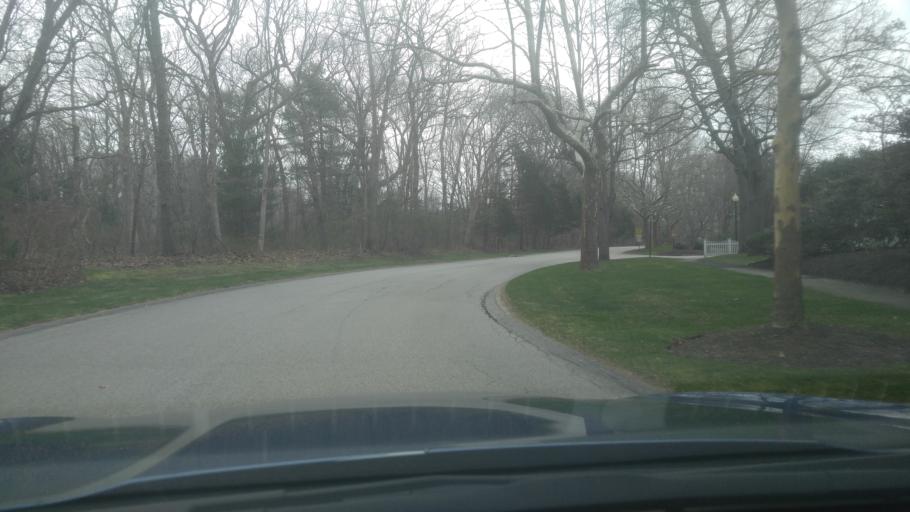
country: US
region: Rhode Island
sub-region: Washington County
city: North Kingstown
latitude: 41.5924
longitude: -71.4452
